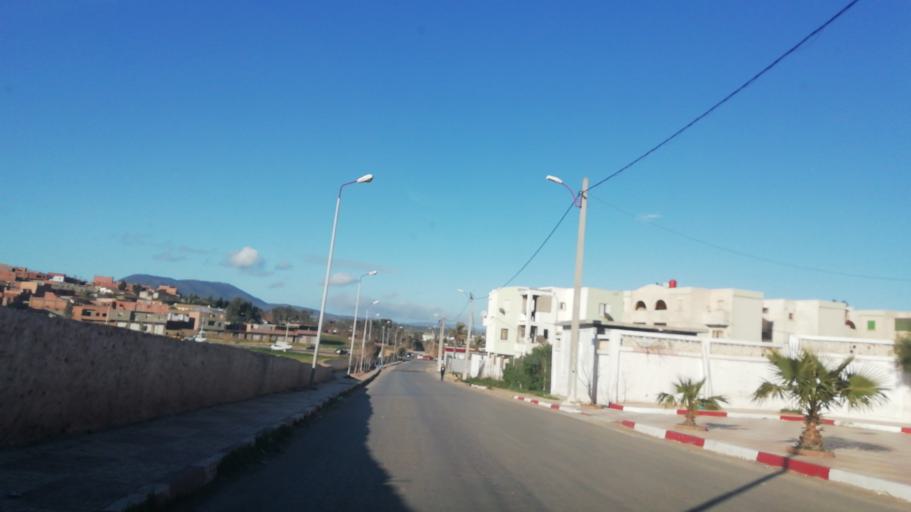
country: DZ
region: Oran
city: Sidi ech Chahmi
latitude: 35.6961
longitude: -0.4942
